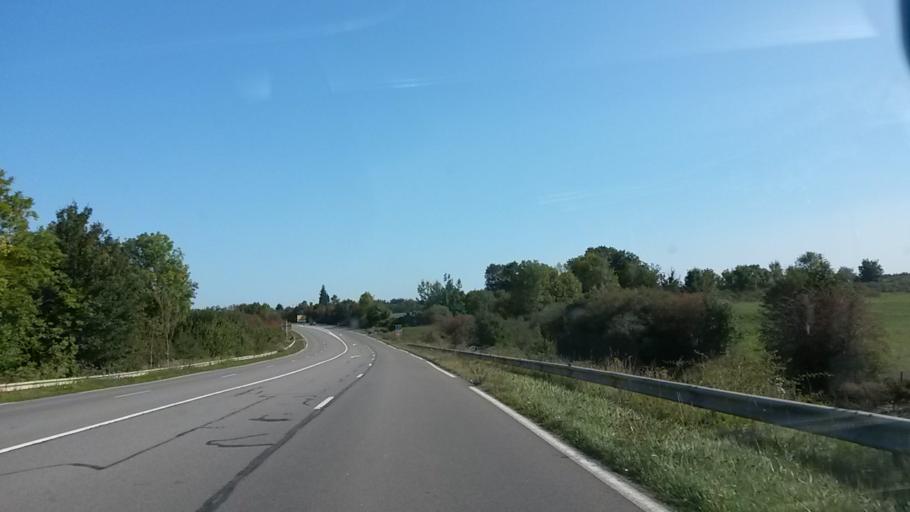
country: FR
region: Picardie
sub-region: Departement de l'Aisne
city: La Flamengrie
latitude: 50.0534
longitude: 3.9304
